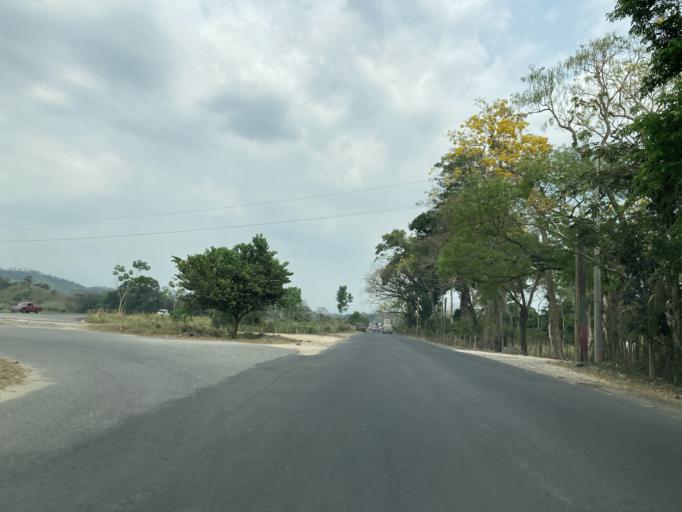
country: GT
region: Suchitepeque
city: Rio Bravo
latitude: 14.4115
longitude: -91.3408
